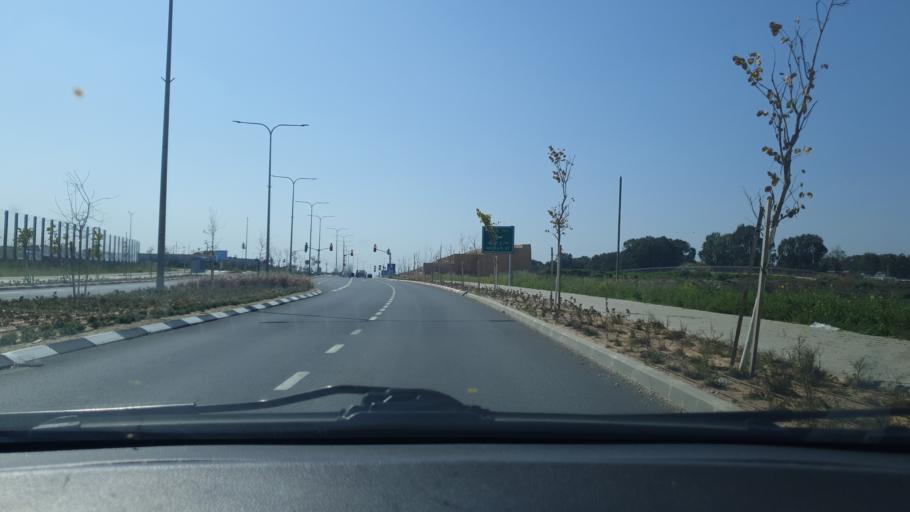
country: IL
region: Central District
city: Ramla
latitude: 31.9312
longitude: 34.8462
